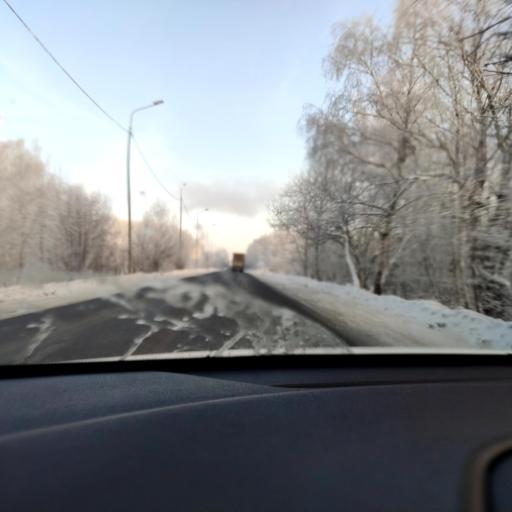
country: RU
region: Tatarstan
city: Staroye Arakchino
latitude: 55.8842
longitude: 48.9871
